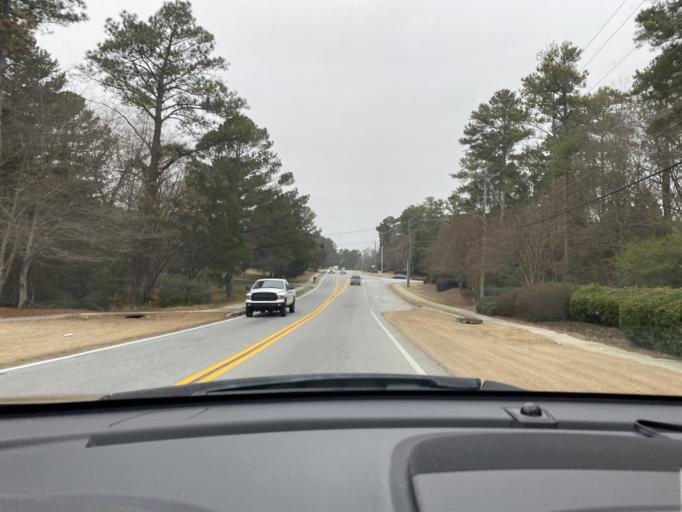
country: US
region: Georgia
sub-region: Gwinnett County
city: Grayson
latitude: 33.9189
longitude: -83.9063
